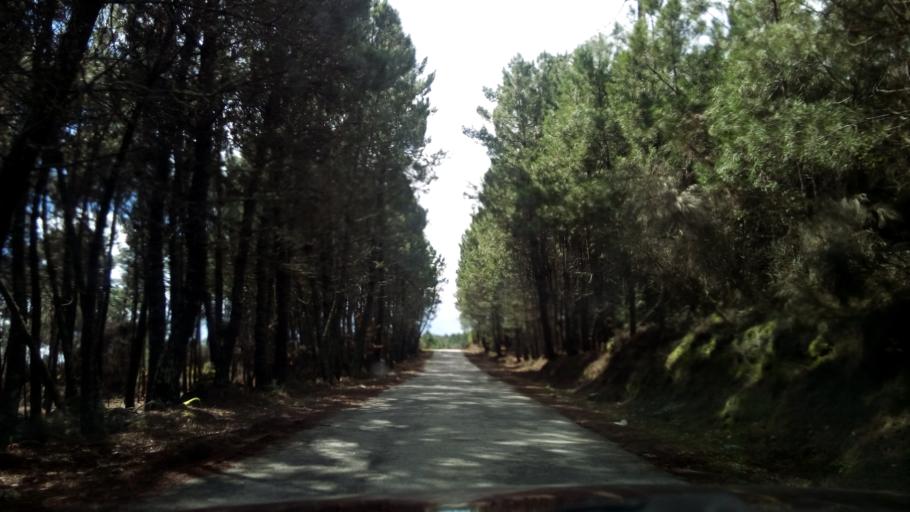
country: PT
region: Guarda
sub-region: Fornos de Algodres
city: Fornos de Algodres
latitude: 40.6555
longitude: -7.5075
